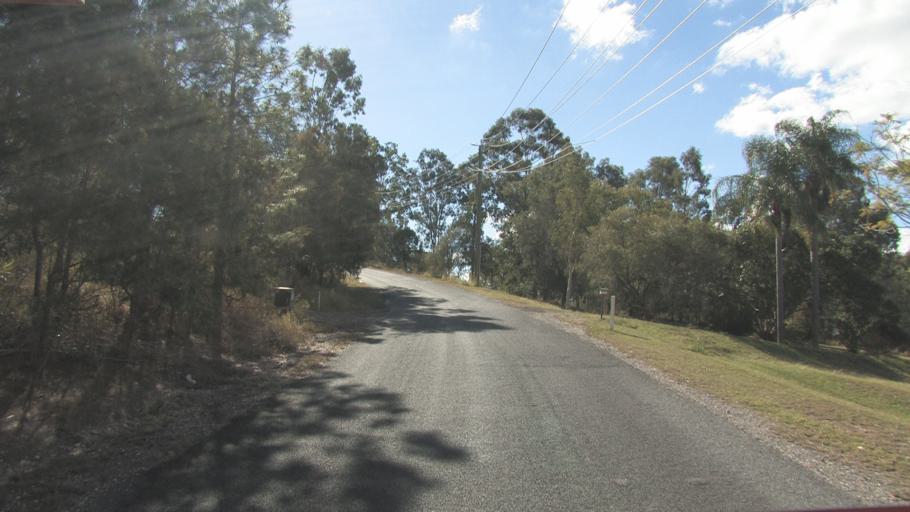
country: AU
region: Queensland
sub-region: Logan
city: Chambers Flat
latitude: -27.8114
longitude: 153.0893
